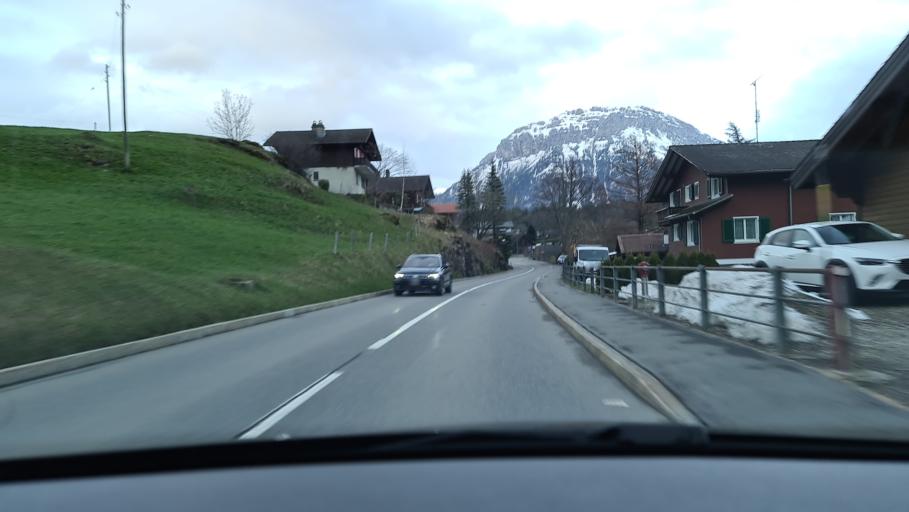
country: CH
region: Uri
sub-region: Uri
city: Bauen
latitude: 46.9637
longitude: 8.5749
